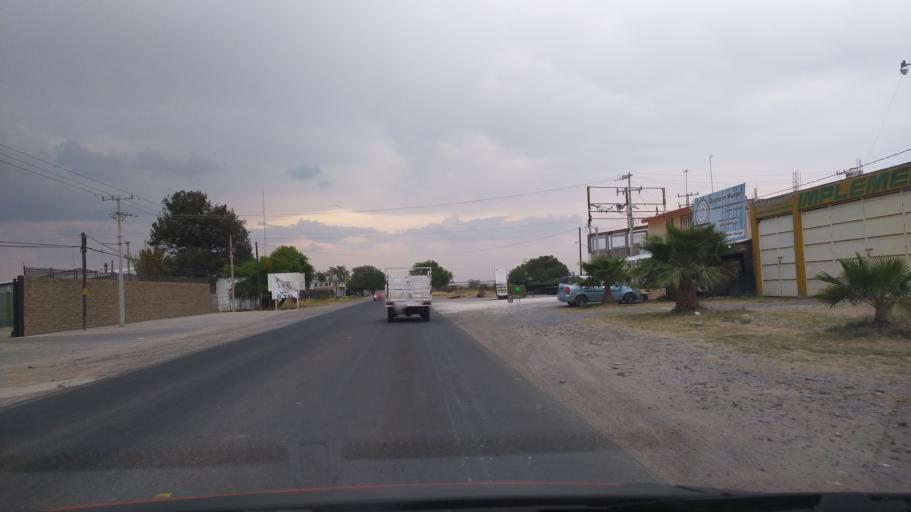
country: MX
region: Guanajuato
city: Ciudad Manuel Doblado
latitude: 20.7322
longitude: -101.9375
